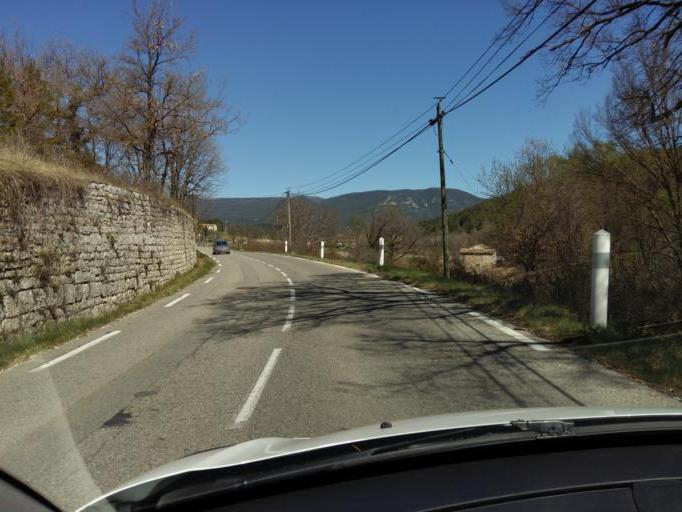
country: FR
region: Provence-Alpes-Cote d'Azur
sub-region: Departement du Vaucluse
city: Apt
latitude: 43.8931
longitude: 5.4296
